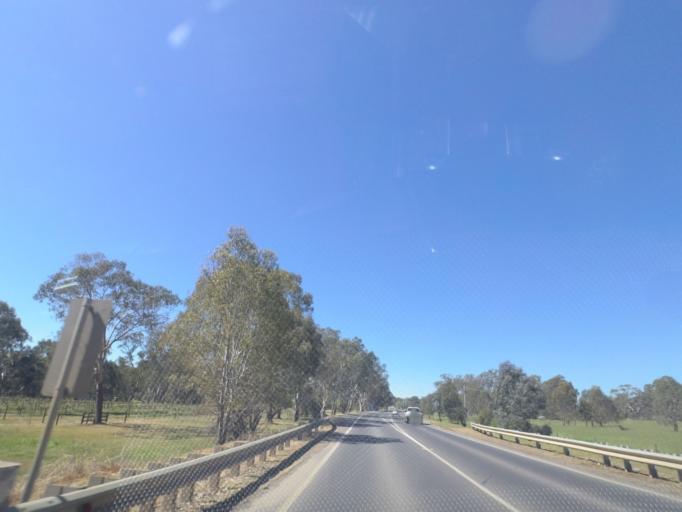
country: AU
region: Victoria
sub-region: Murrindindi
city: Kinglake West
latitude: -37.0245
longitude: 145.1126
